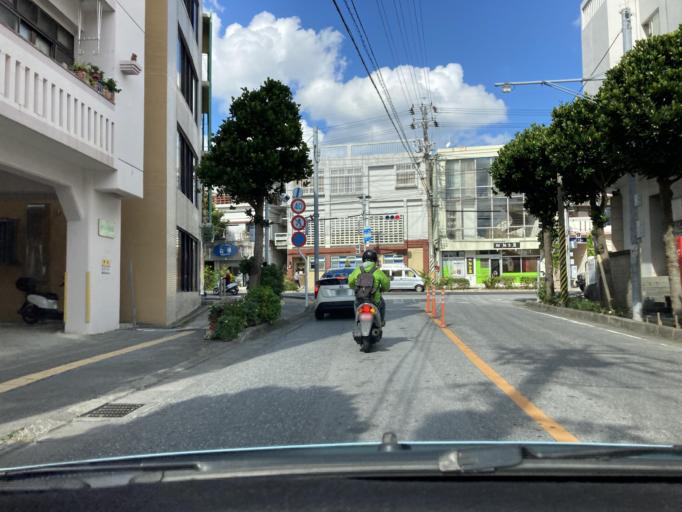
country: JP
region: Okinawa
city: Naha-shi
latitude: 26.2170
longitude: 127.6998
